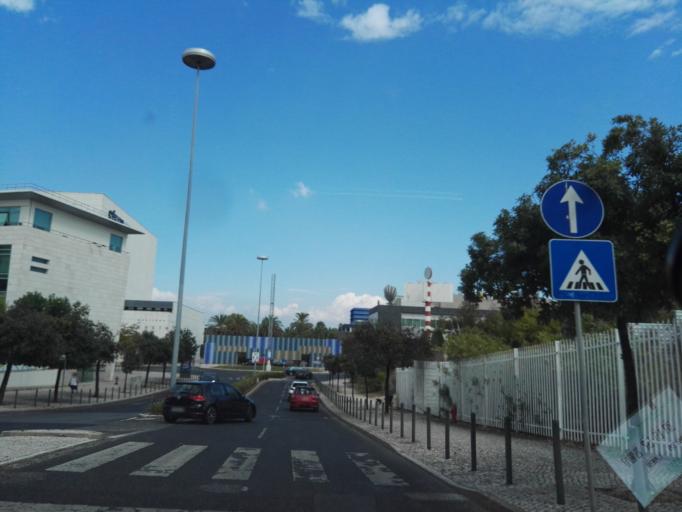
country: PT
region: Lisbon
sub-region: Loures
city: Moscavide
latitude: 38.7616
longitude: -9.0975
